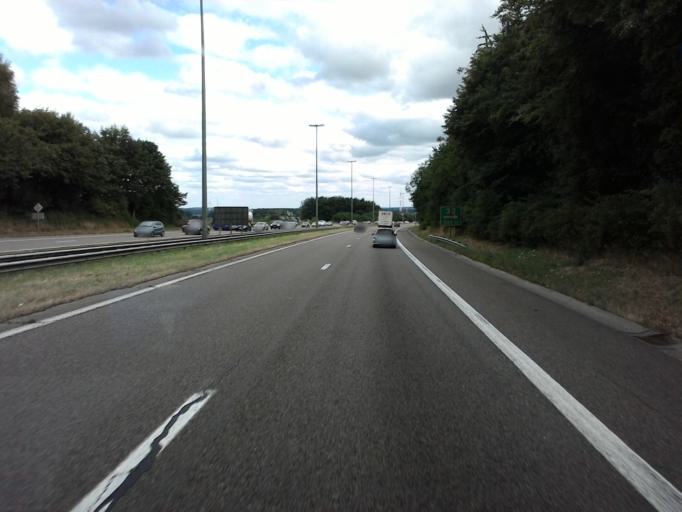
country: BE
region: Wallonia
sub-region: Province du Luxembourg
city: Arlon
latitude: 49.6612
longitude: 5.8131
